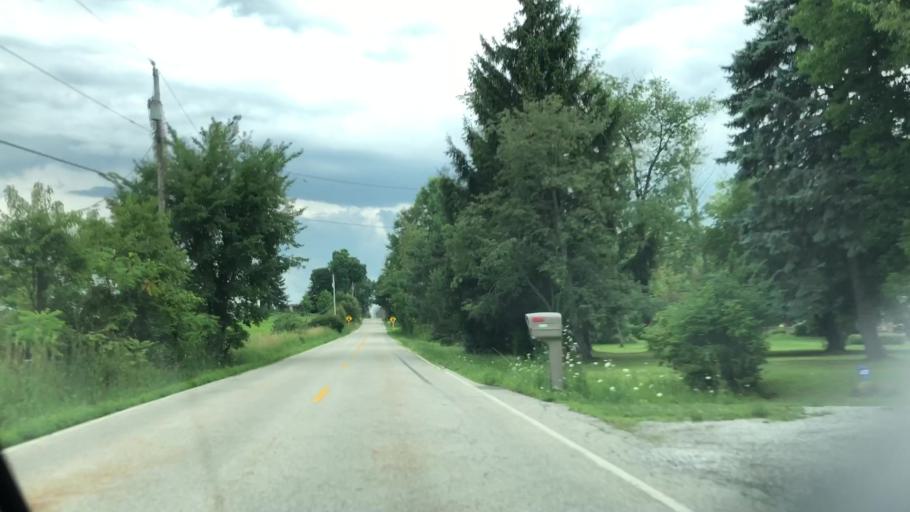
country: US
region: Ohio
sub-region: Summit County
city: Montrose-Ghent
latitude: 41.1208
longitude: -81.7159
